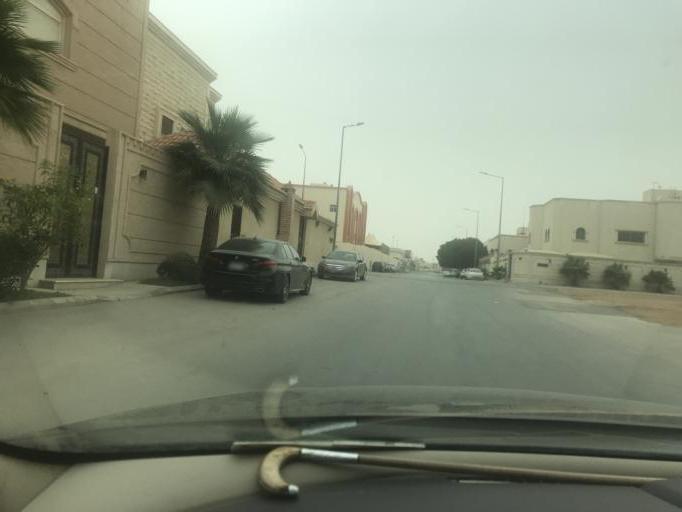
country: SA
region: Ar Riyad
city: Riyadh
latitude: 24.7265
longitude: 46.7877
